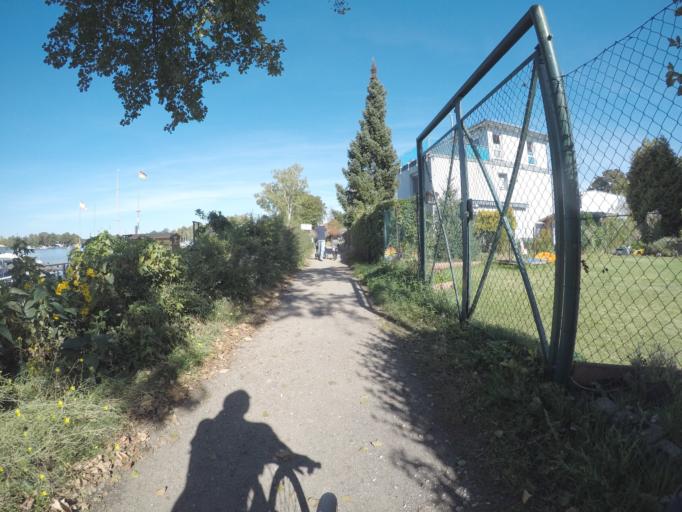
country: DE
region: Berlin
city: Konradshohe
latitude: 52.5695
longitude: 13.2285
